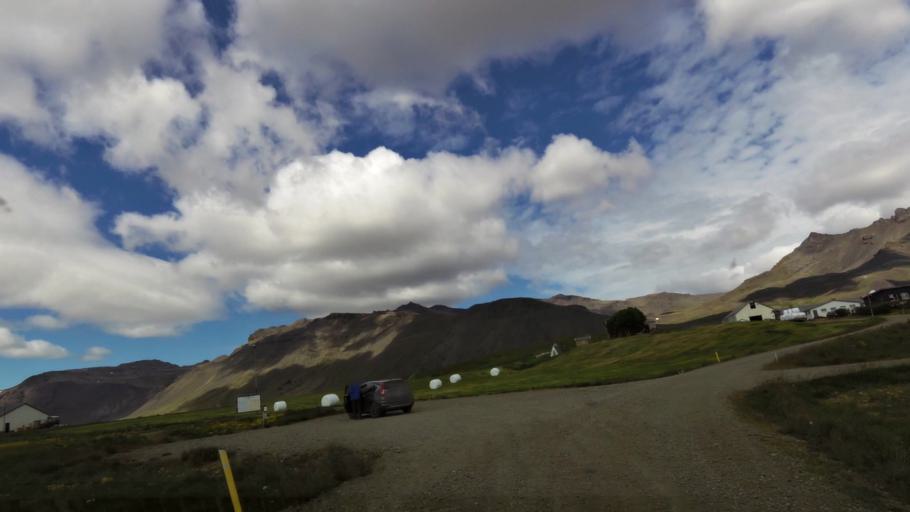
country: IS
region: West
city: Stykkisholmur
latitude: 64.8362
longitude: -22.9759
